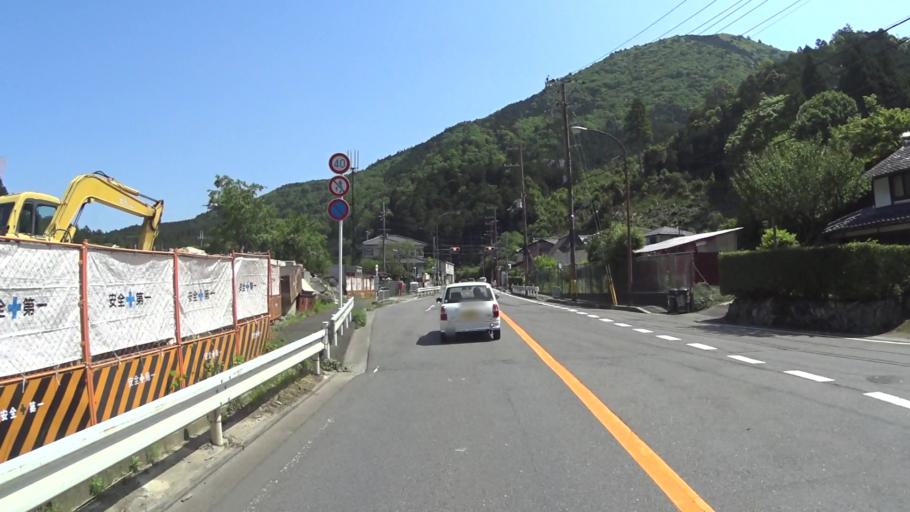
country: JP
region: Kyoto
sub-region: Kyoto-shi
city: Kamigyo-ku
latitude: 35.0874
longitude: 135.8205
